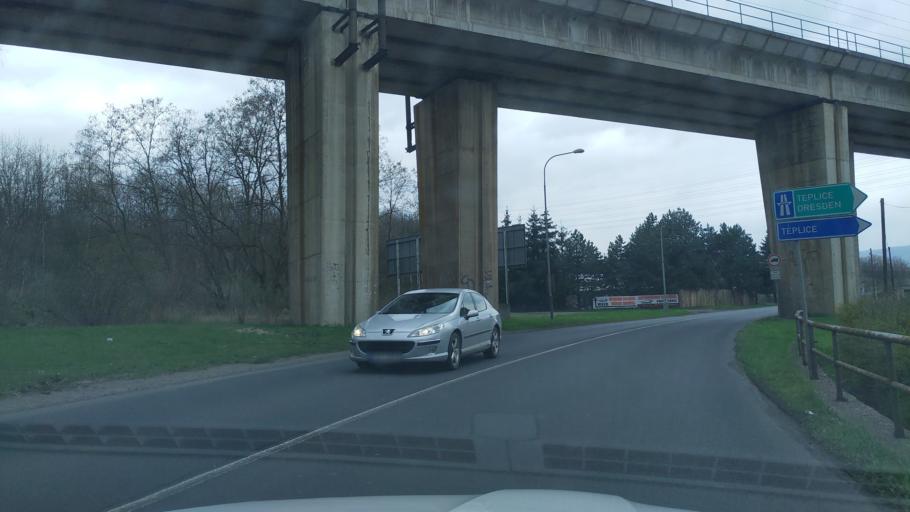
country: CZ
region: Ustecky
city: Trmice
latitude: 50.6595
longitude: 13.9840
